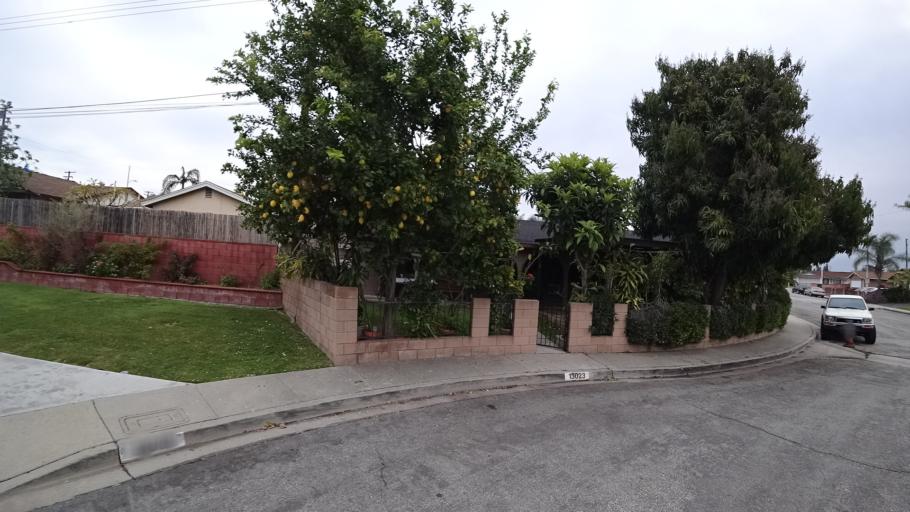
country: US
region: California
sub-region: Los Angeles County
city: Avocado Heights
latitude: 34.0628
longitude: -117.9934
